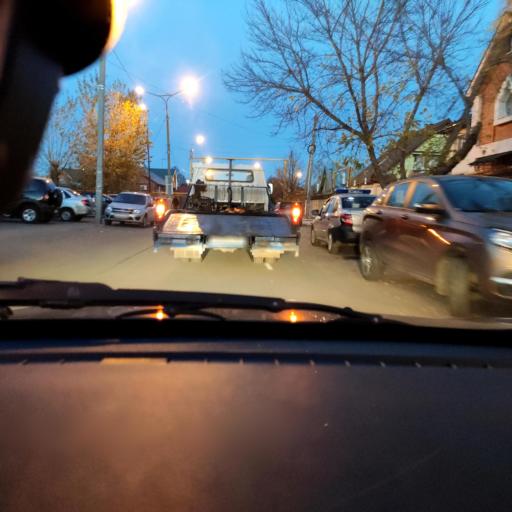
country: RU
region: Samara
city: Tol'yatti
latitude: 53.5242
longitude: 49.4068
